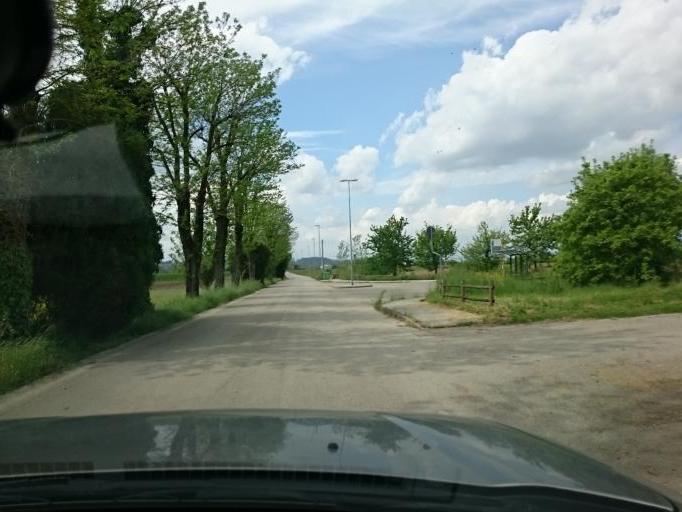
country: IT
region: Veneto
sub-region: Provincia di Vicenza
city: Longare
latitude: 45.4987
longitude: 11.5938
